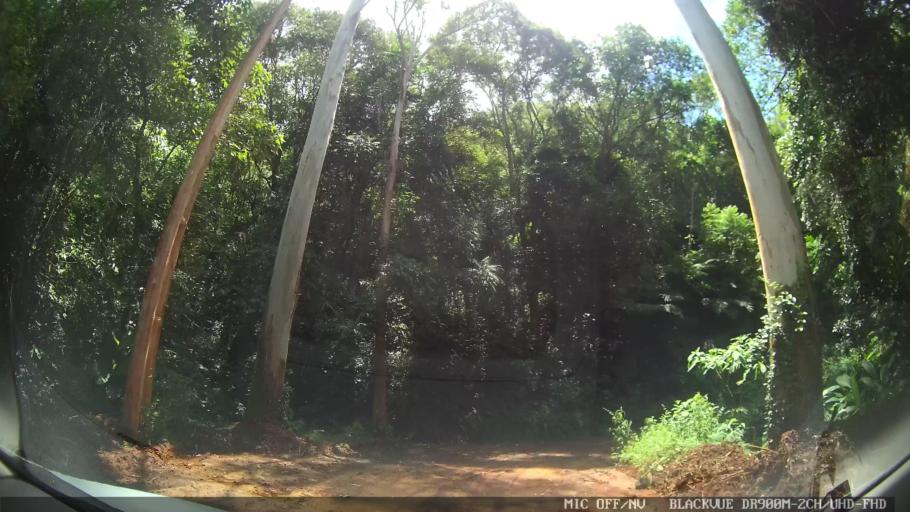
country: BR
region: Minas Gerais
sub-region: Extrema
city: Extrema
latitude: -22.8777
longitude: -46.2939
